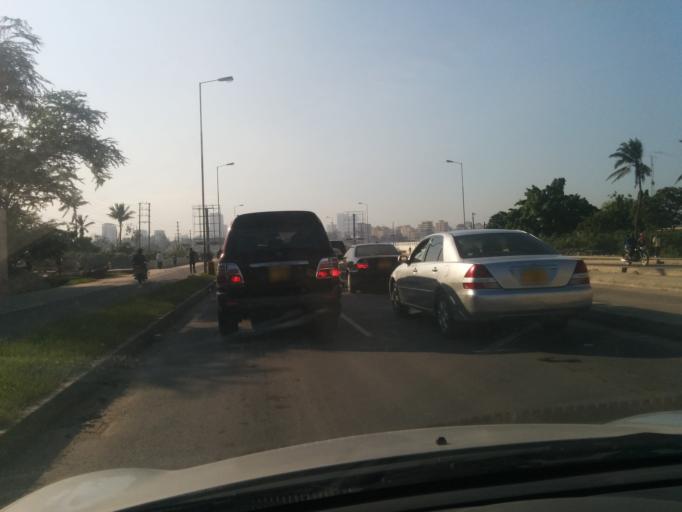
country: TZ
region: Dar es Salaam
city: Dar es Salaam
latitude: -6.8098
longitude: 39.2646
